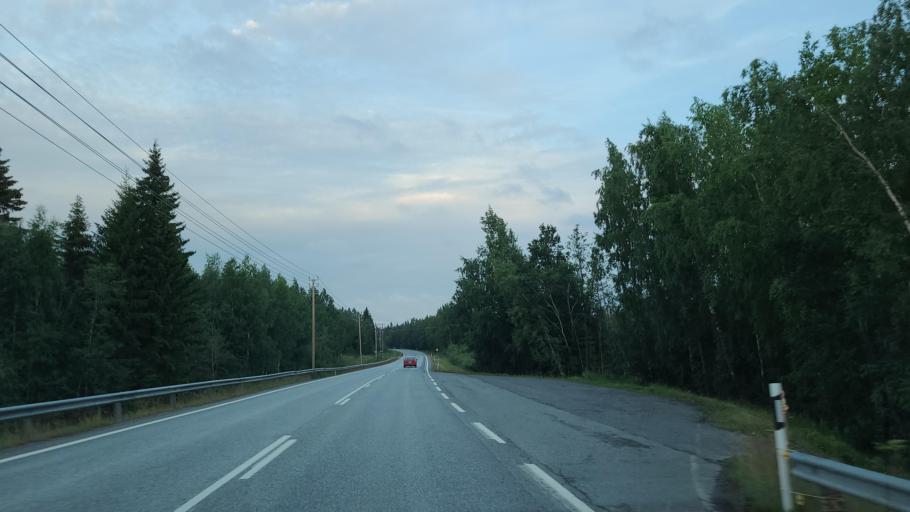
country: FI
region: Ostrobothnia
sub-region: Vaasa
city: Vaasa
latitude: 63.1888
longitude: 21.5650
